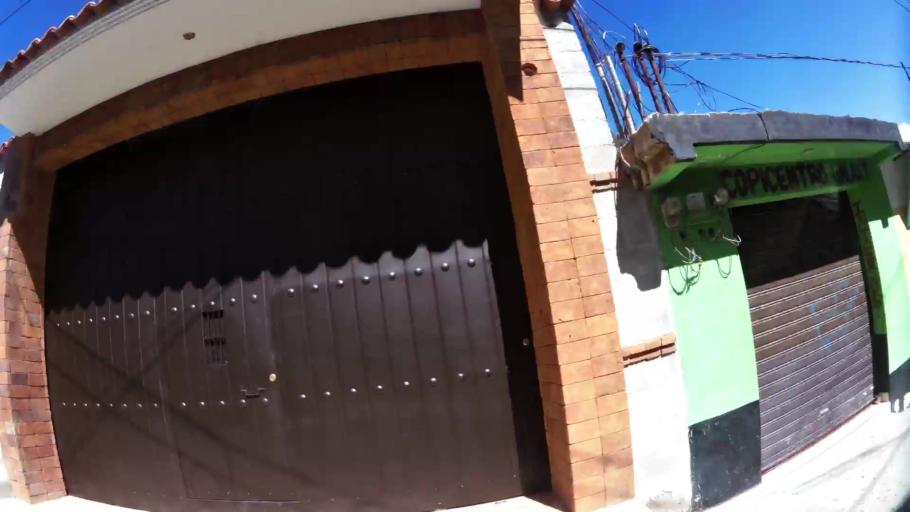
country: GT
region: Solola
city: Solola
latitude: 14.7729
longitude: -91.1842
